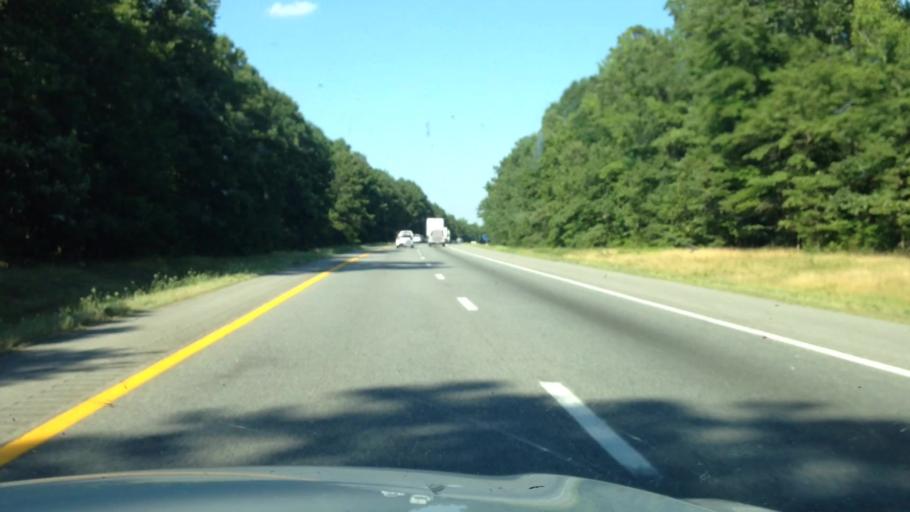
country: US
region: Virginia
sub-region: City of Emporia
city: Emporia
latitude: 36.7576
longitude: -77.5029
